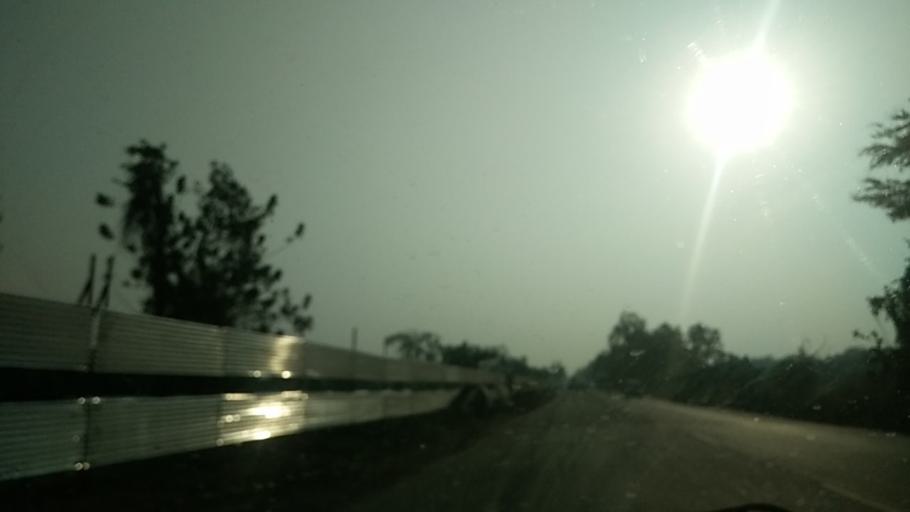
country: IN
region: Goa
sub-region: North Goa
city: Guirim
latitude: 15.5811
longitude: 73.8138
